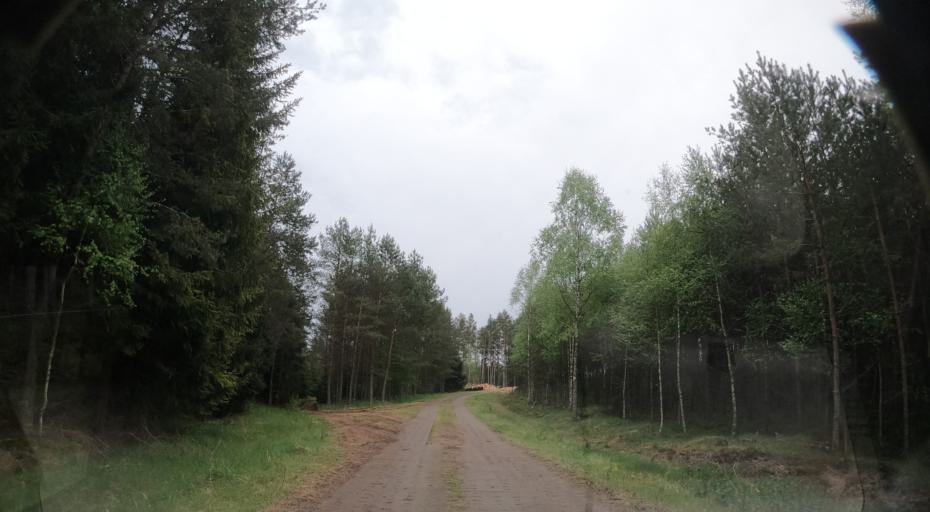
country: PL
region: West Pomeranian Voivodeship
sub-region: Powiat koszalinski
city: Bobolice
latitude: 54.0613
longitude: 16.4233
